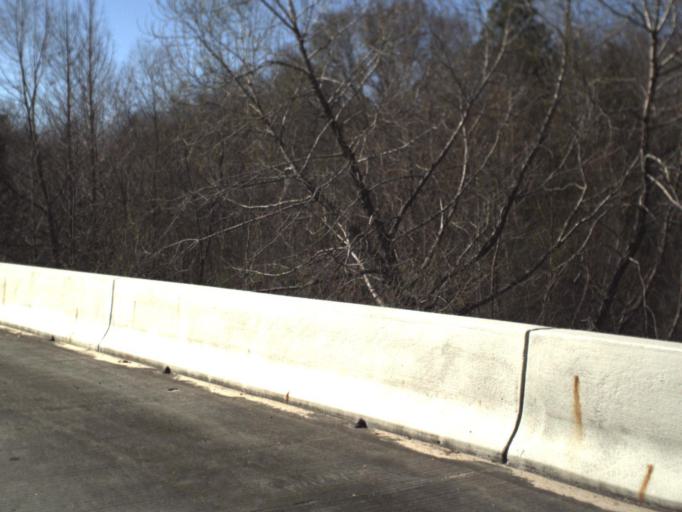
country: US
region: Florida
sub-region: Calhoun County
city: Blountstown
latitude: 30.4432
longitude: -85.0381
